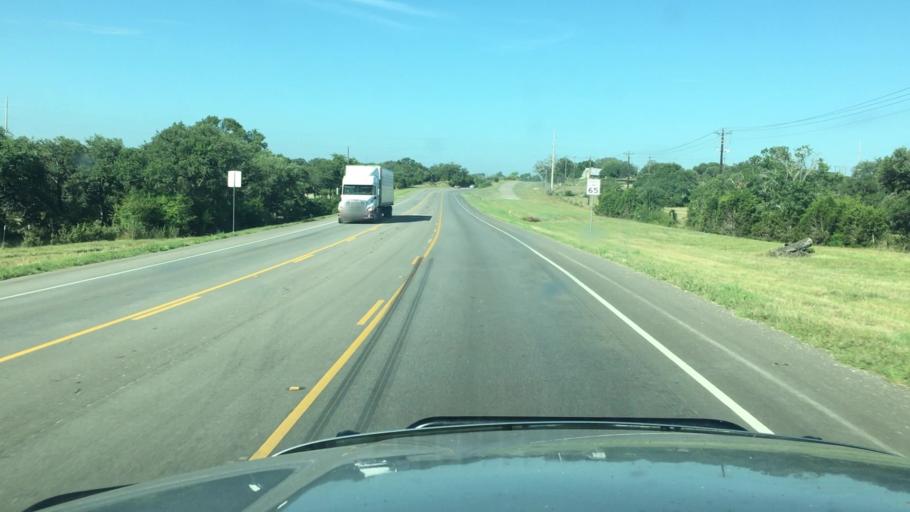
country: US
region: Texas
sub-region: Hays County
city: Dripping Springs
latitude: 30.2040
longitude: -98.1511
